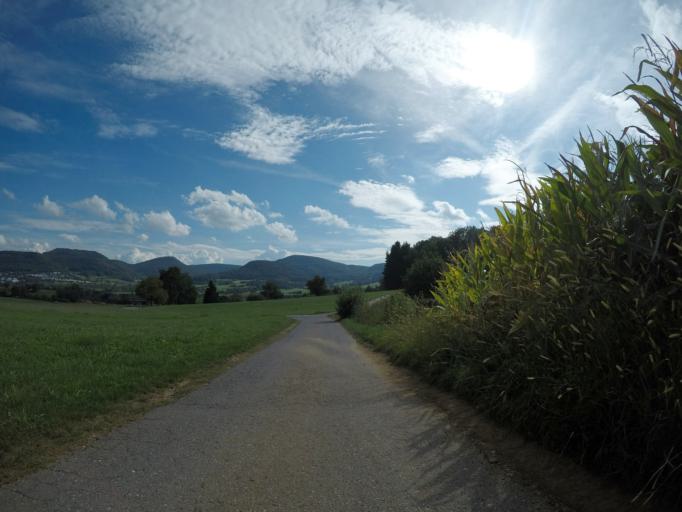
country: DE
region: Baden-Wuerttemberg
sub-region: Tuebingen Region
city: Reutlingen
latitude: 48.4590
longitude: 9.1935
